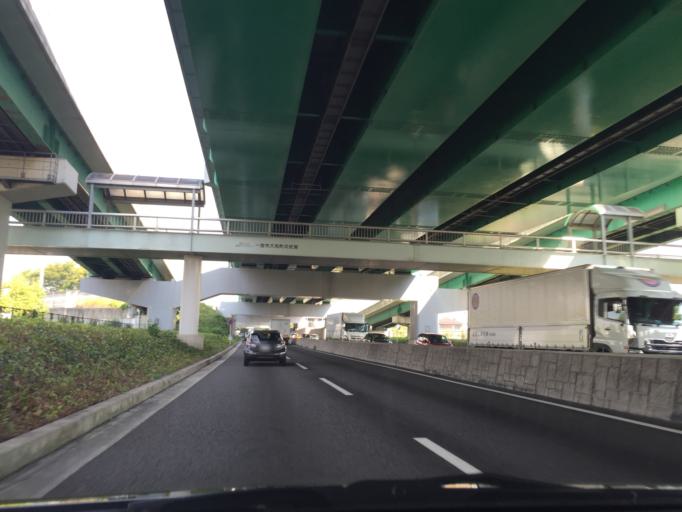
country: JP
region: Aichi
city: Ichinomiya
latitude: 35.2920
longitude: 136.7796
